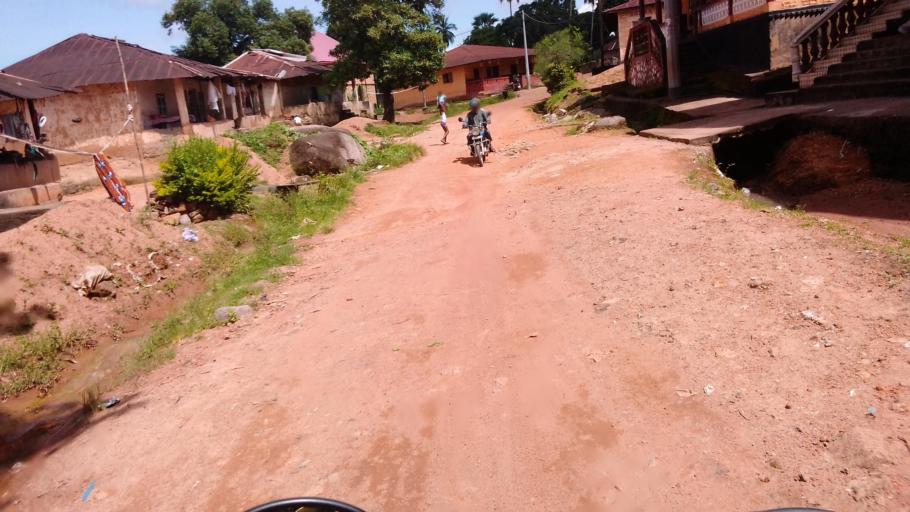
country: SL
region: Northern Province
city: Makeni
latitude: 8.8860
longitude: -12.0422
